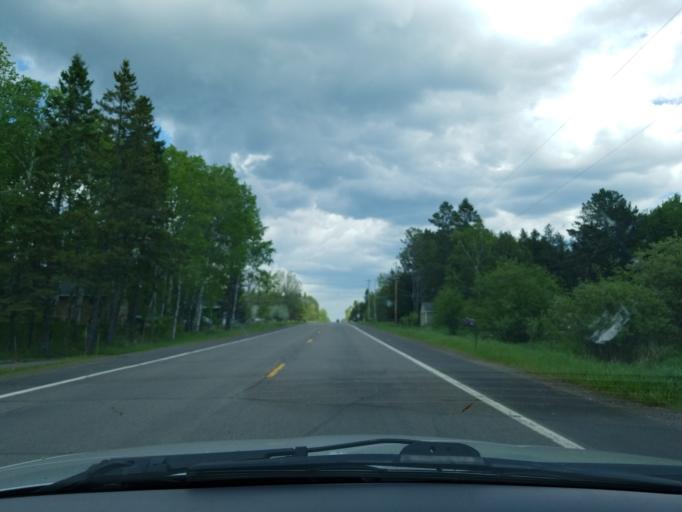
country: US
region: Minnesota
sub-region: Saint Louis County
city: Proctor
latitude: 46.7786
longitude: -92.2083
